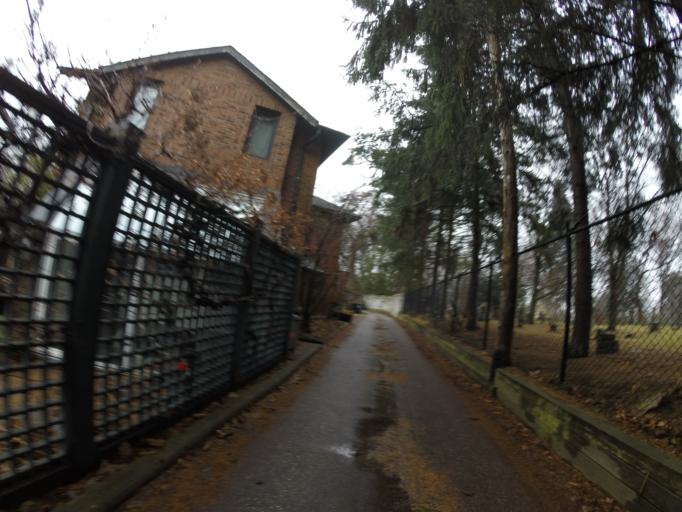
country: CA
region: Ontario
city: Toronto
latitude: 43.6685
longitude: -79.3628
